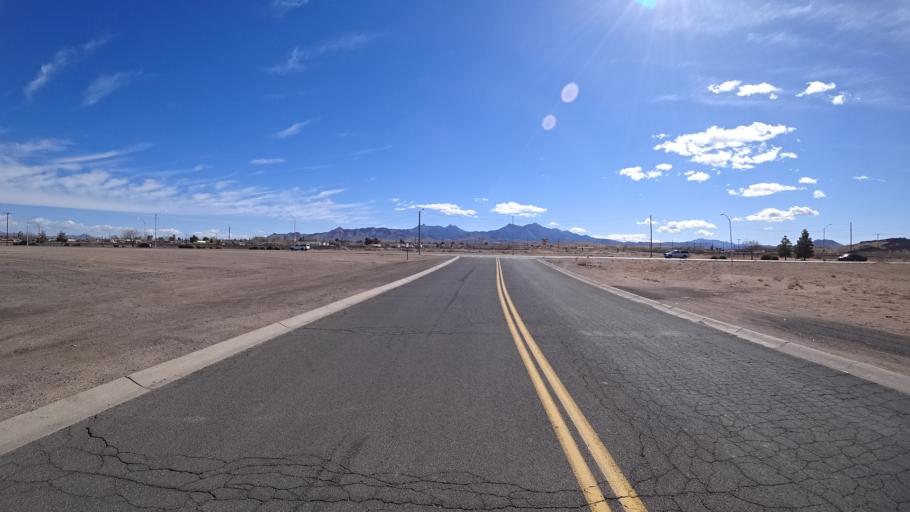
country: US
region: Arizona
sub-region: Mohave County
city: Kingman
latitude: 35.1983
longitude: -114.0286
